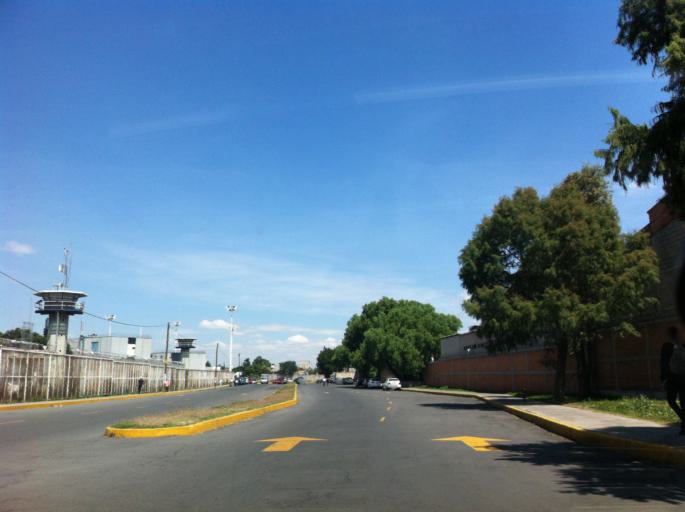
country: MX
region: Mexico
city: Los Reyes La Paz
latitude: 19.3557
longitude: -99.0089
